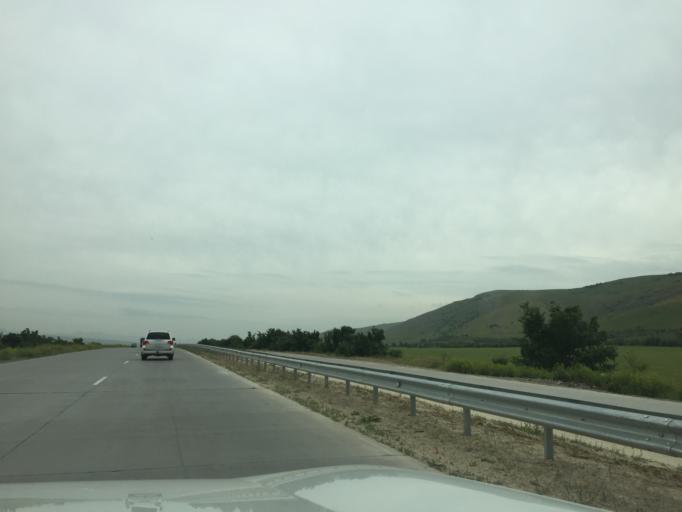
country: KZ
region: Ongtustik Qazaqstan
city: Sastobe
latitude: 42.5429
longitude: 70.0546
